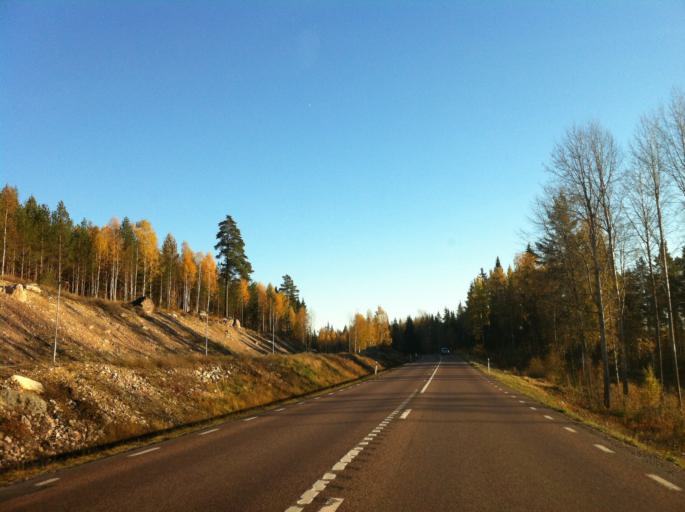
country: SE
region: Dalarna
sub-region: Faluns Kommun
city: Grycksbo
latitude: 60.6756
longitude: 15.5106
